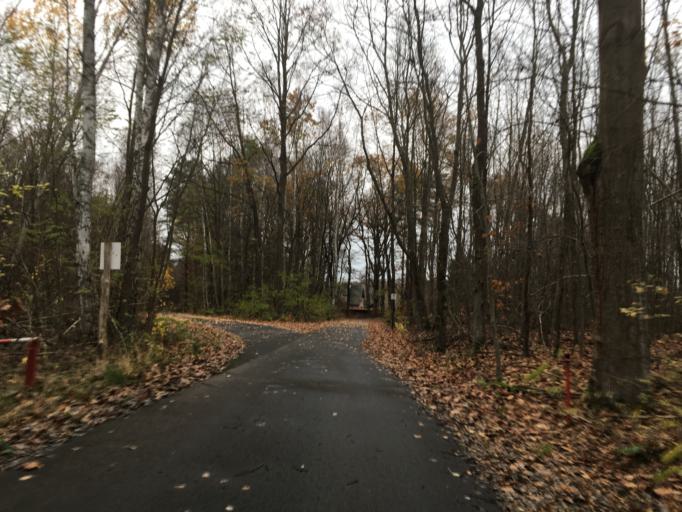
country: DE
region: Brandenburg
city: Mullrose
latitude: 52.2414
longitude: 14.4498
